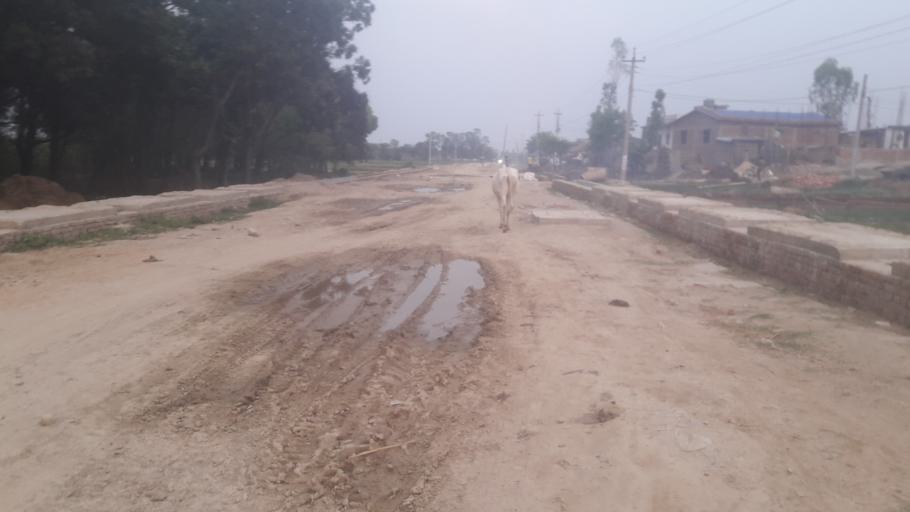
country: NP
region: Eastern Region
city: Siraha
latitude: 26.6565
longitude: 86.1956
